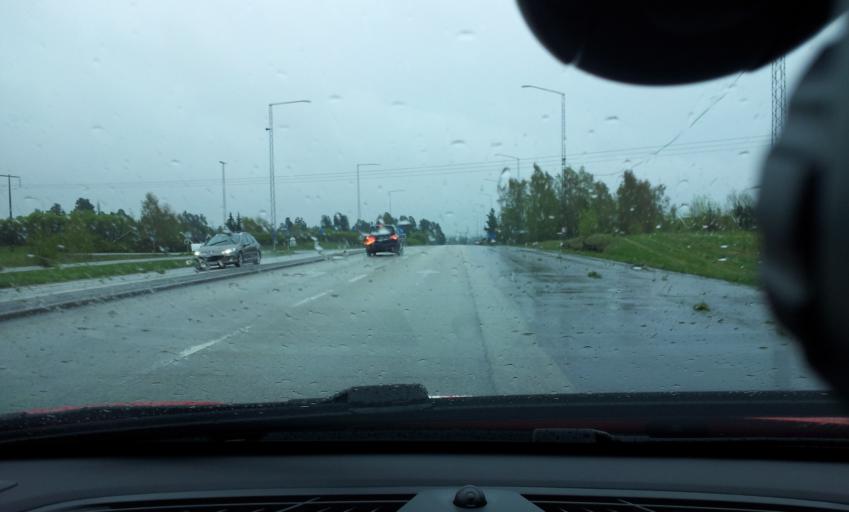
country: SE
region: Jaemtland
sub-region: OEstersunds Kommun
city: Ostersund
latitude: 63.1499
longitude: 14.7048
